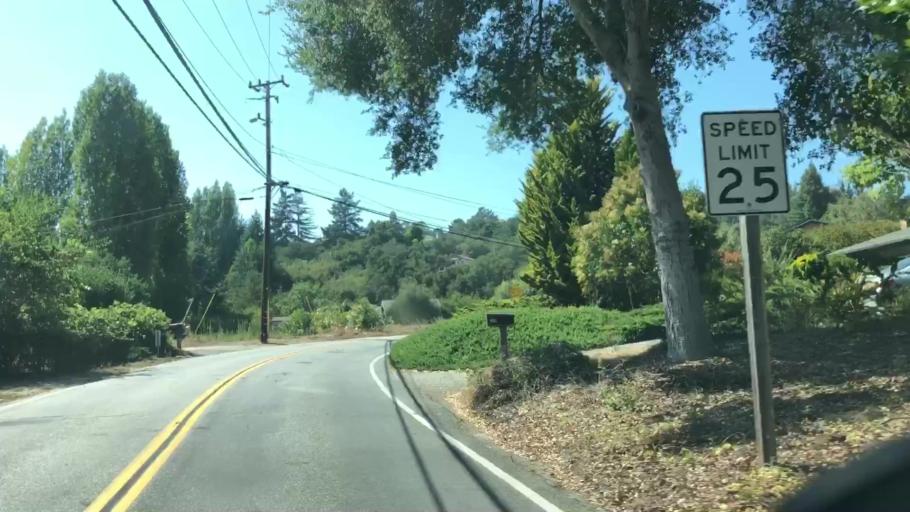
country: US
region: California
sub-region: Santa Cruz County
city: Corralitos
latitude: 36.9933
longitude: -121.8150
